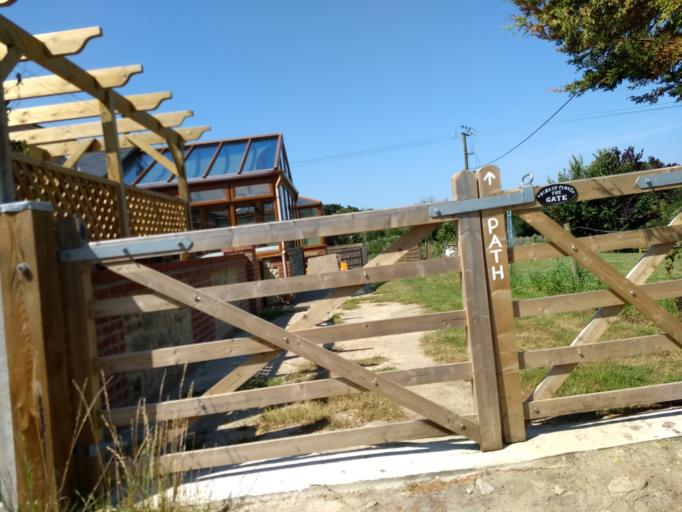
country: GB
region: England
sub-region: Isle of Wight
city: Newport
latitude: 50.6952
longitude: -1.3289
